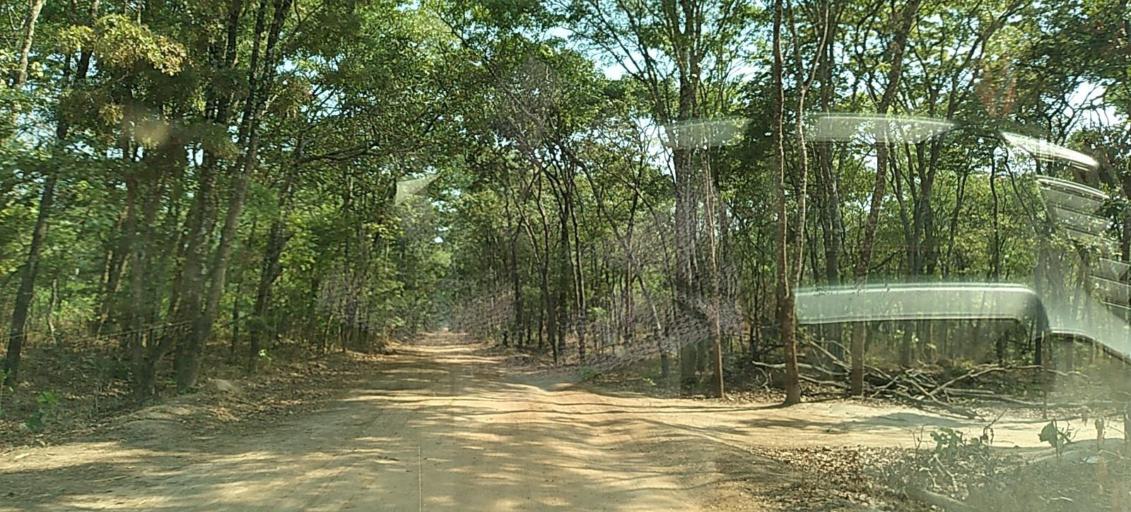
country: ZM
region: Copperbelt
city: Kalulushi
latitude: -12.9225
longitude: 27.8223
